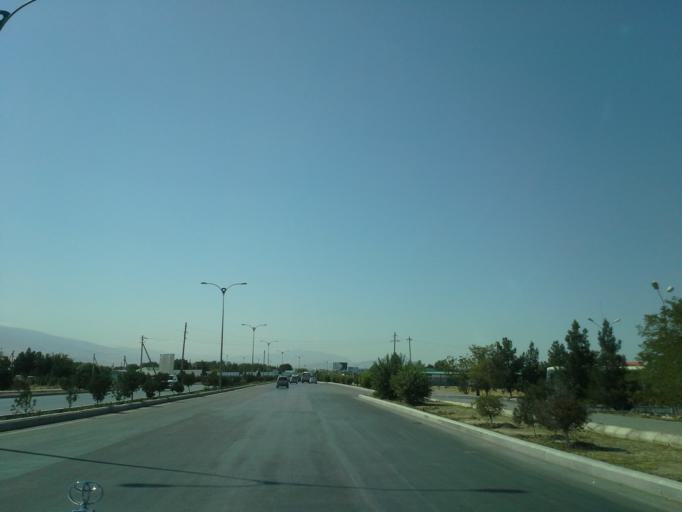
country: TM
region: Ahal
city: Annau
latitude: 37.9074
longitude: 58.5145
